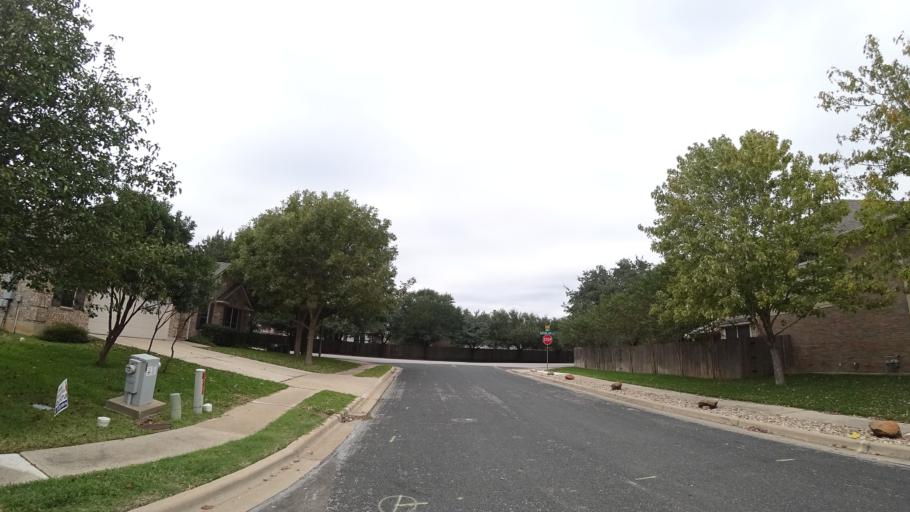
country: US
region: Texas
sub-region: Travis County
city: Shady Hollow
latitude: 30.1528
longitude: -97.8554
